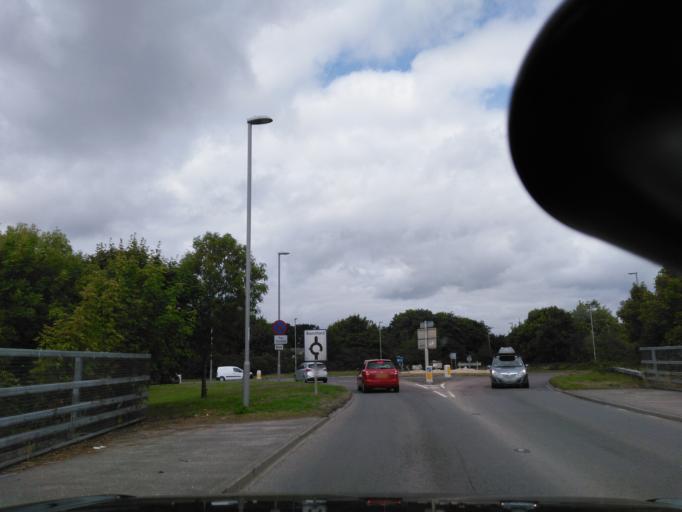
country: GB
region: England
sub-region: Dorset
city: Wareham
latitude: 50.6943
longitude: -2.1131
